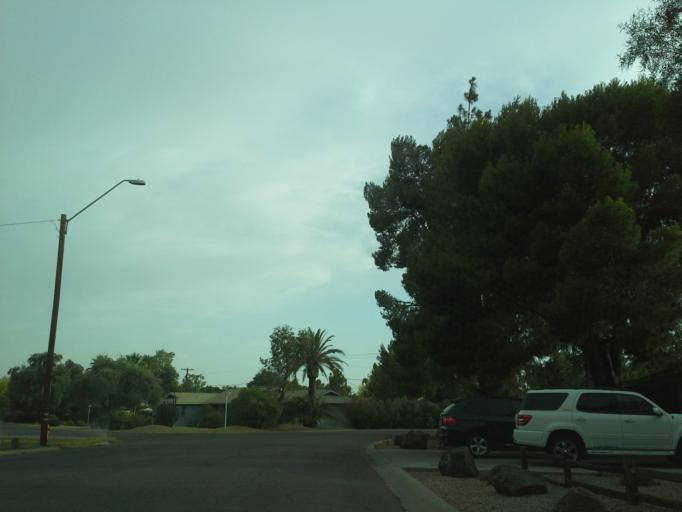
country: US
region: Arizona
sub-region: Maricopa County
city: Phoenix
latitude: 33.5280
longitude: -112.0858
